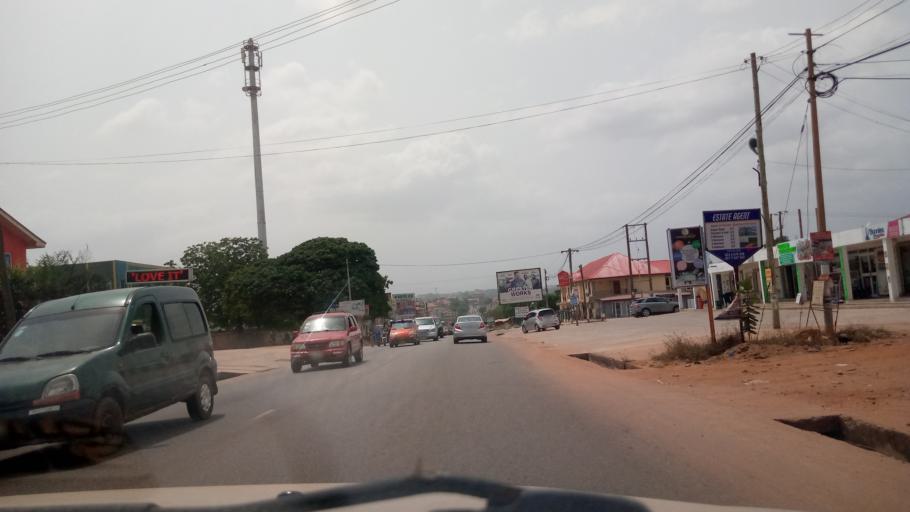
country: GH
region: Greater Accra
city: Medina Estates
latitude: 5.6819
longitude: -0.1930
